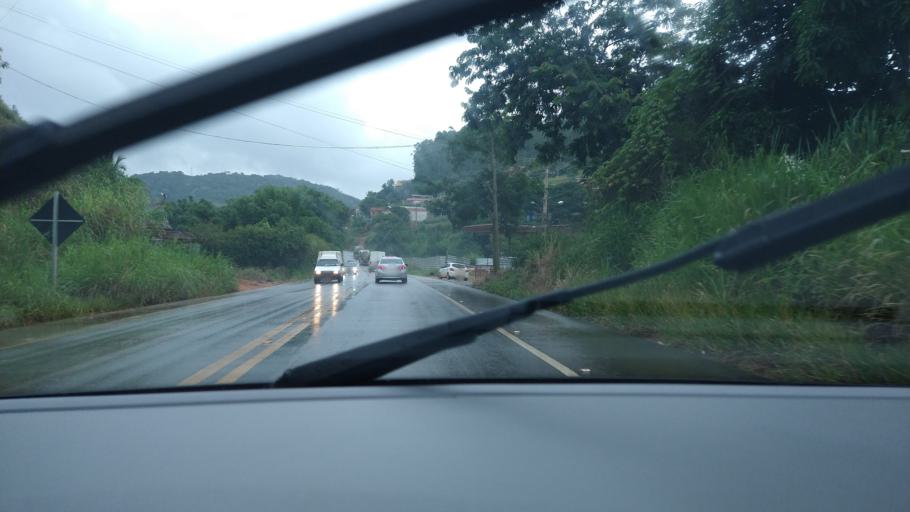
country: BR
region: Minas Gerais
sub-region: Vicosa
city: Vicosa
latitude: -20.6396
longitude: -42.8663
